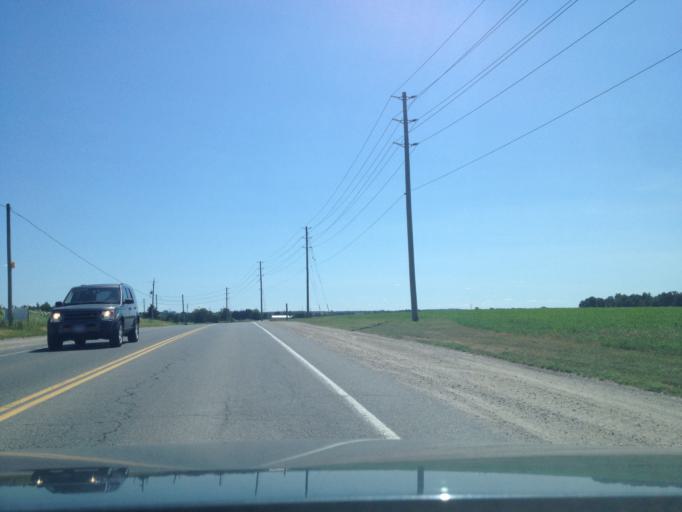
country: CA
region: Ontario
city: Waterloo
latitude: 43.5338
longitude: -80.5126
